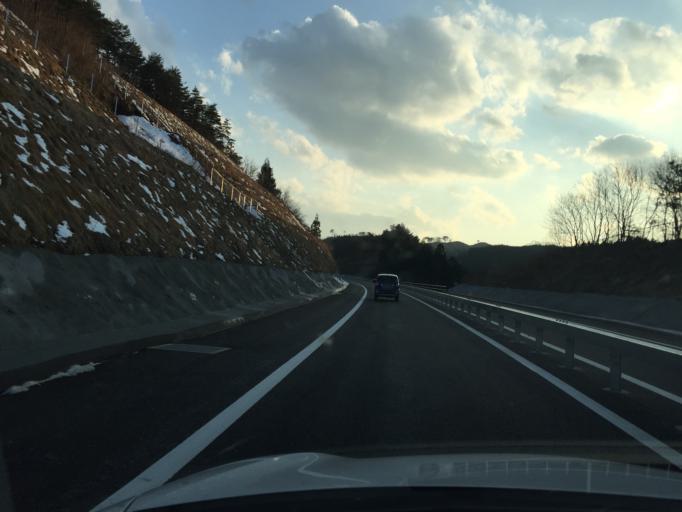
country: JP
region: Miyagi
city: Marumori
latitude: 37.7889
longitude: 140.7618
